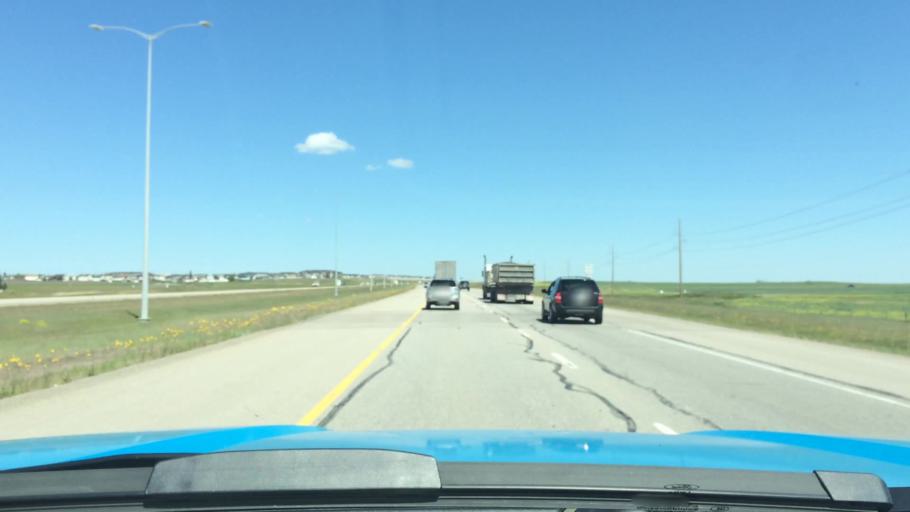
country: CA
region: Alberta
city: Chestermere
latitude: 51.1051
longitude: -113.9188
